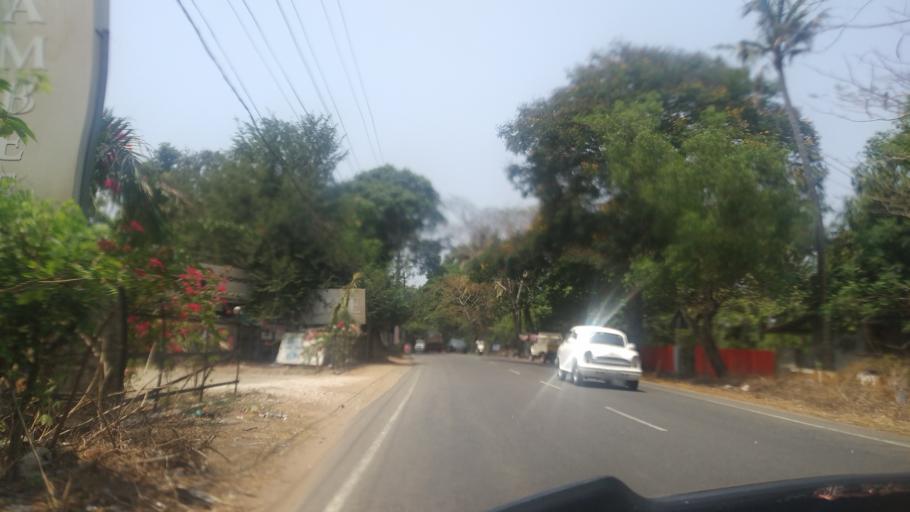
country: IN
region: Kerala
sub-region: Thrissur District
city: Kodungallur
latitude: 10.2669
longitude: 76.1796
